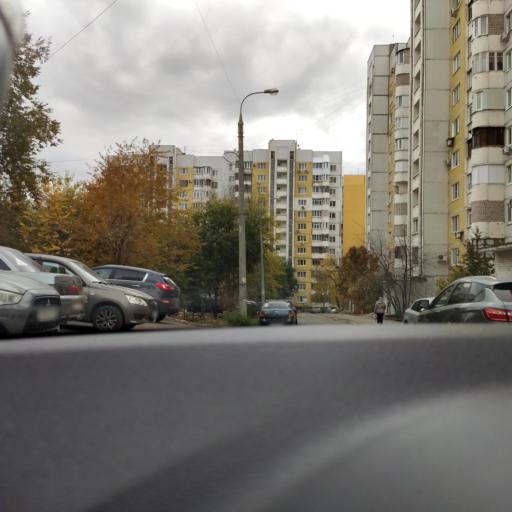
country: RU
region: Samara
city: Samara
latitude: 53.2091
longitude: 50.2146
